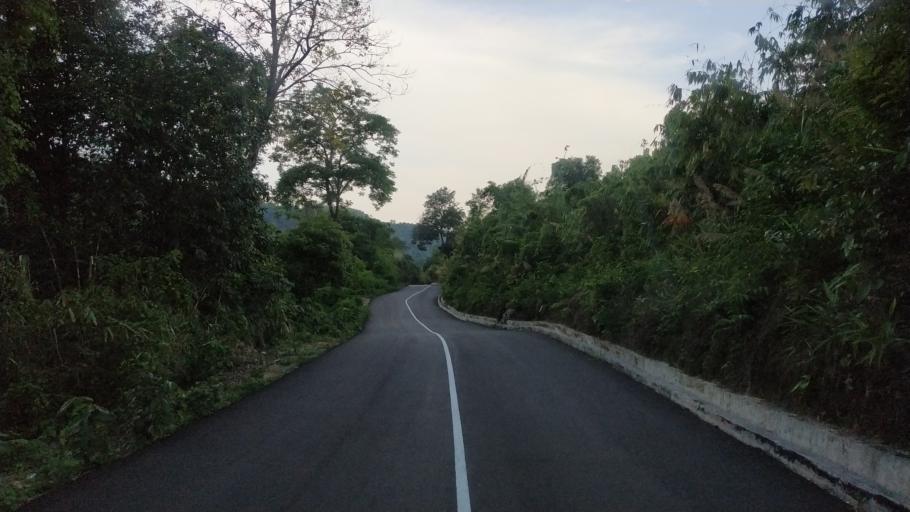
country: MM
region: Mon
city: Kyaikto
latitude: 17.4410
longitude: 97.0978
